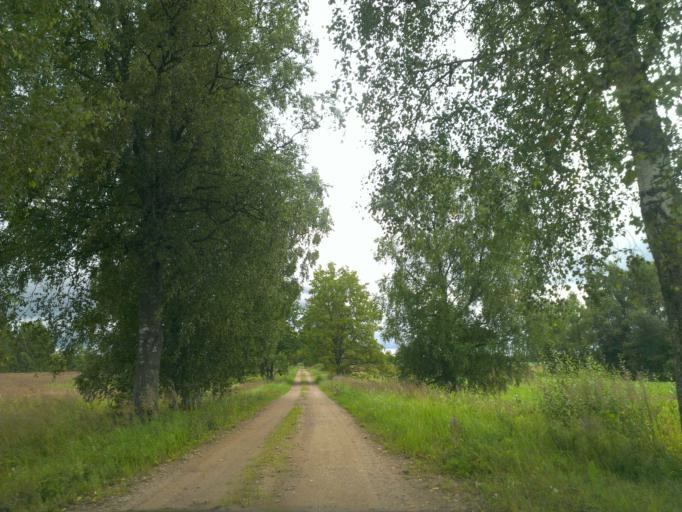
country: LV
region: Sigulda
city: Sigulda
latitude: 57.2214
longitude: 24.9347
